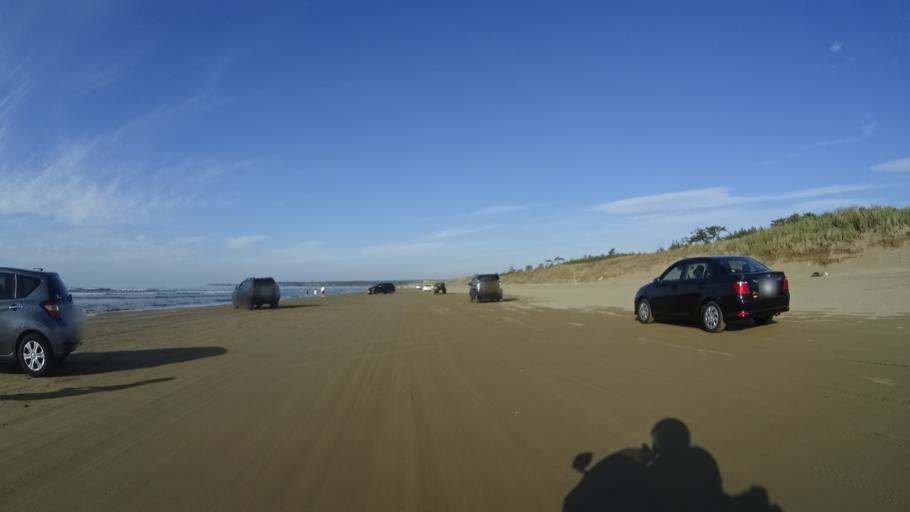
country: JP
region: Ishikawa
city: Hakui
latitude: 36.8847
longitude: 136.7631
